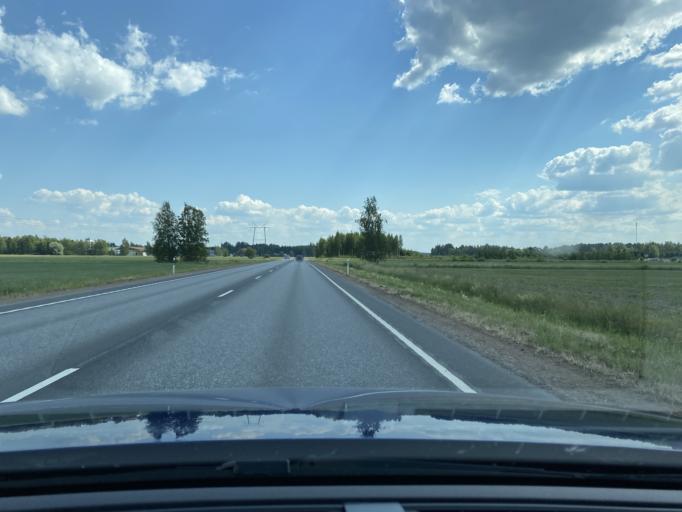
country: FI
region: Satakunta
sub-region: Rauma
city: Eura
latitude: 61.1430
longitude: 22.1099
